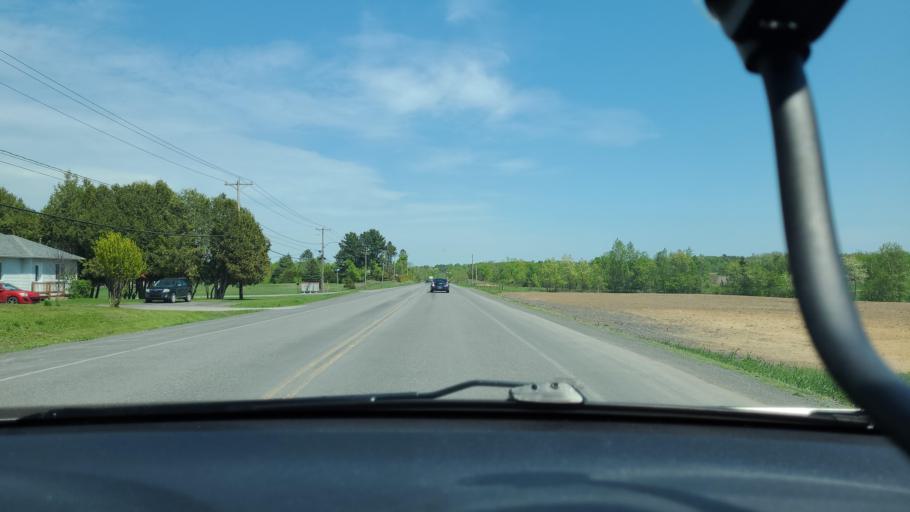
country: CA
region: Quebec
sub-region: Laurentides
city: Lachute
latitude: 45.6680
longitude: -74.2229
